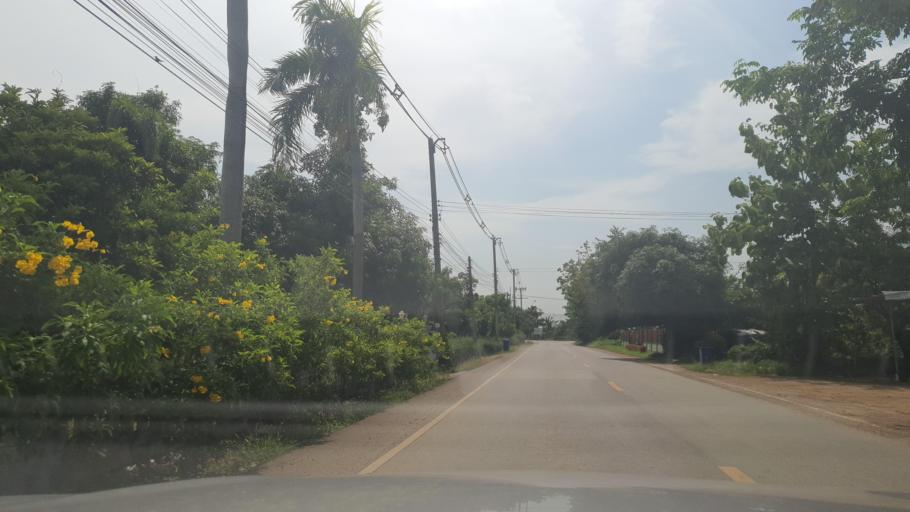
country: TH
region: Sukhothai
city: Si Samrong
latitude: 17.1416
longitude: 99.8252
